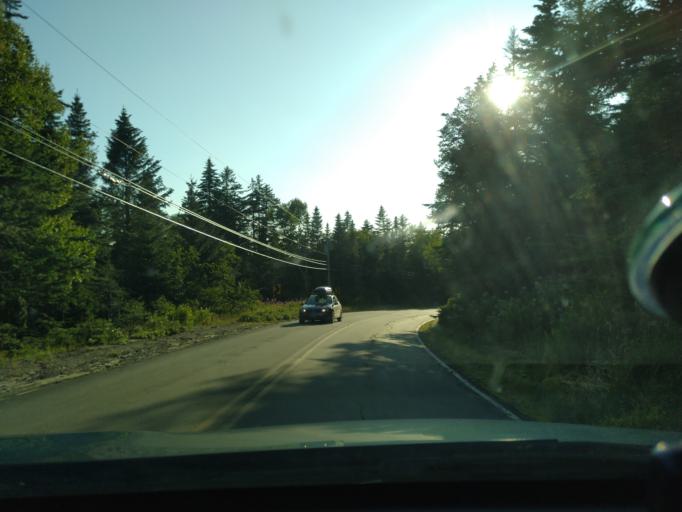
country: US
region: Maine
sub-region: Washington County
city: Machiasport
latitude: 44.6594
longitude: -67.2214
